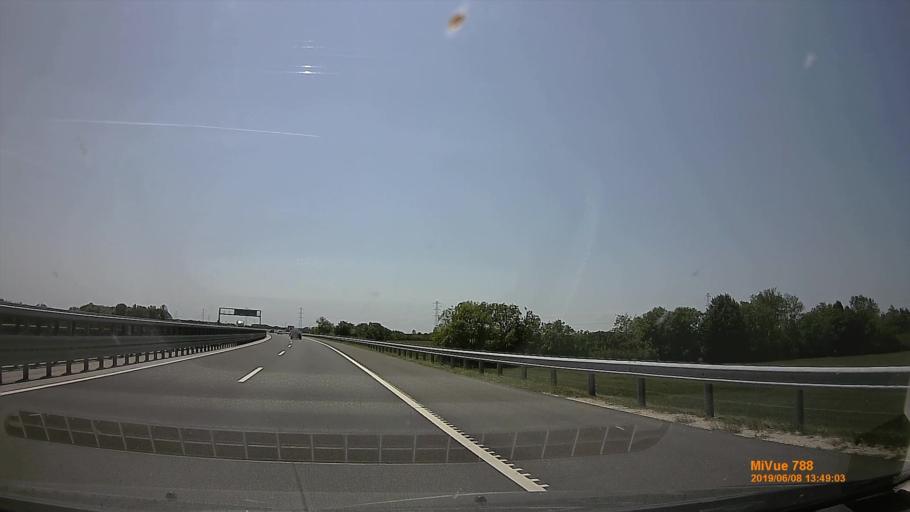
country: HU
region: Vas
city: Repcelak
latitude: 47.4065
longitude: 17.0088
